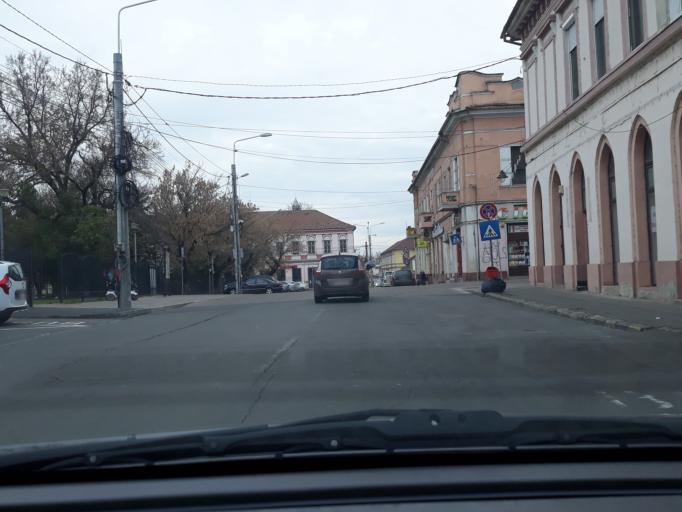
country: RO
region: Bihor
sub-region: Comuna Biharea
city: Oradea
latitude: 47.0539
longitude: 21.9330
